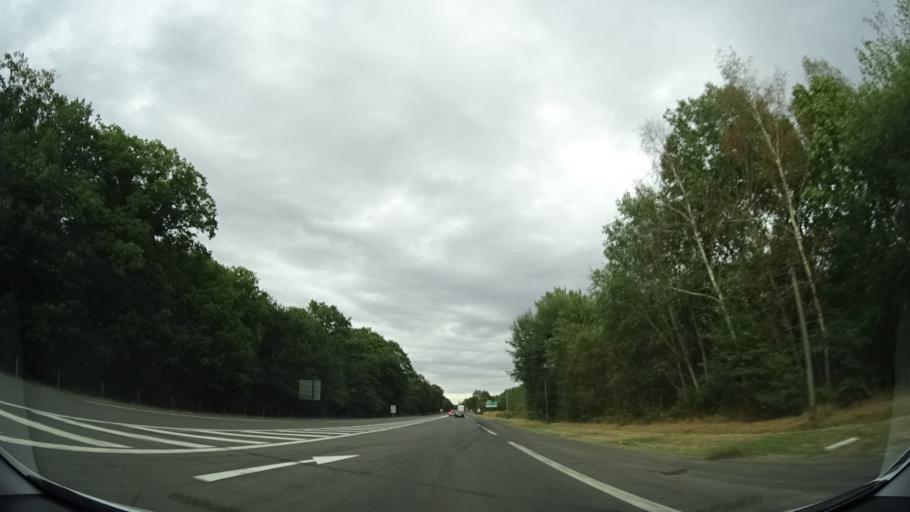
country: FR
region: Centre
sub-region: Departement du Loiret
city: Chateauneuf-sur-Loire
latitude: 47.8839
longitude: 2.2426
